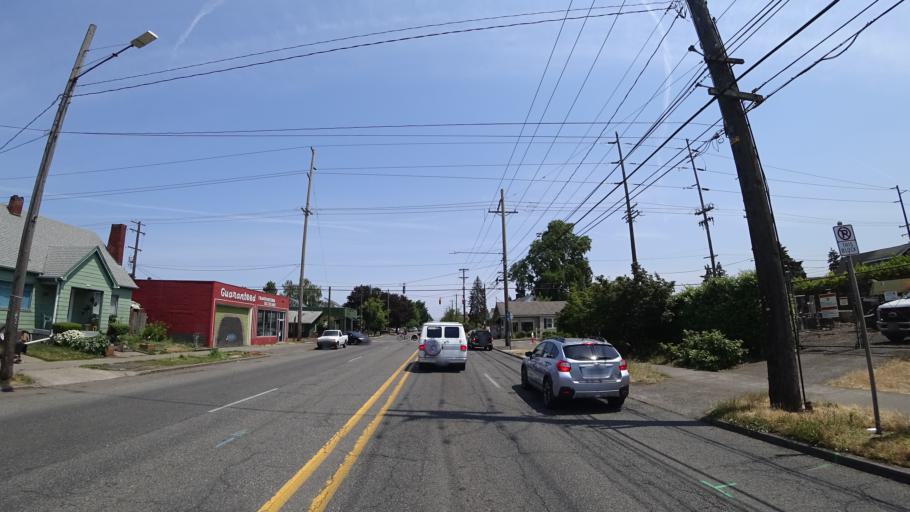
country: US
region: Oregon
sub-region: Multnomah County
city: Portland
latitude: 45.5771
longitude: -122.6931
